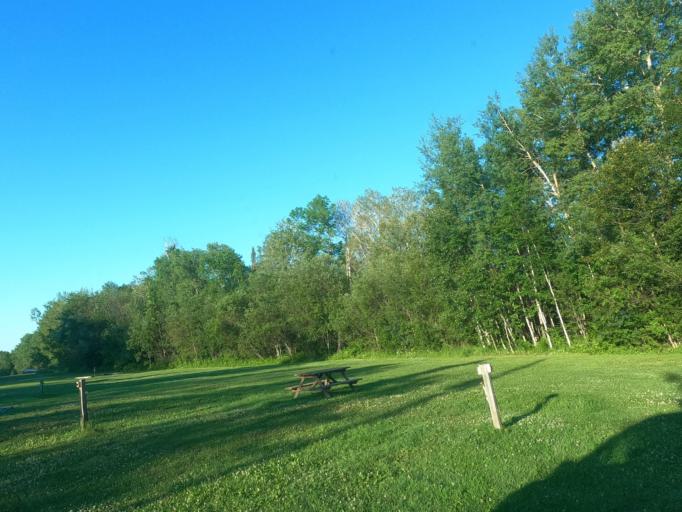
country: CA
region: Ontario
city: Dryden
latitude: 49.8239
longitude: -93.3397
